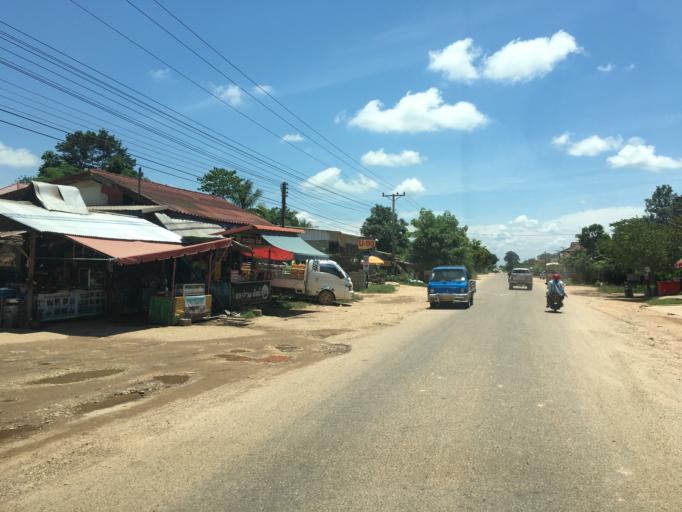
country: LA
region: Vientiane
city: Muang Phon-Hong
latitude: 18.2649
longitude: 102.4840
